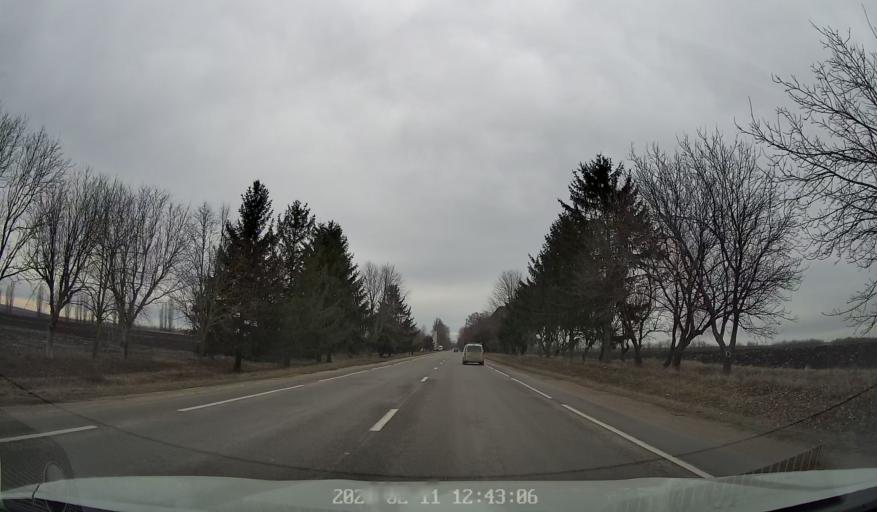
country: MD
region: Raionul Edinet
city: Edinet
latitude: 48.2292
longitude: 27.2140
